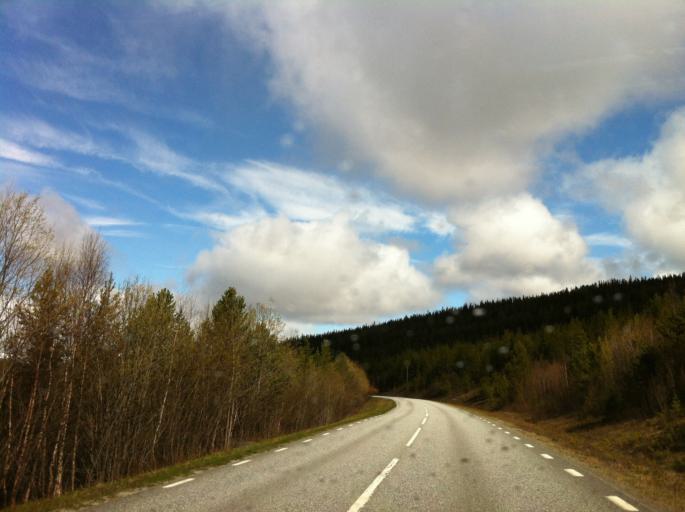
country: SE
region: Jaemtland
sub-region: Are Kommun
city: Are
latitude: 62.5784
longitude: 12.5593
